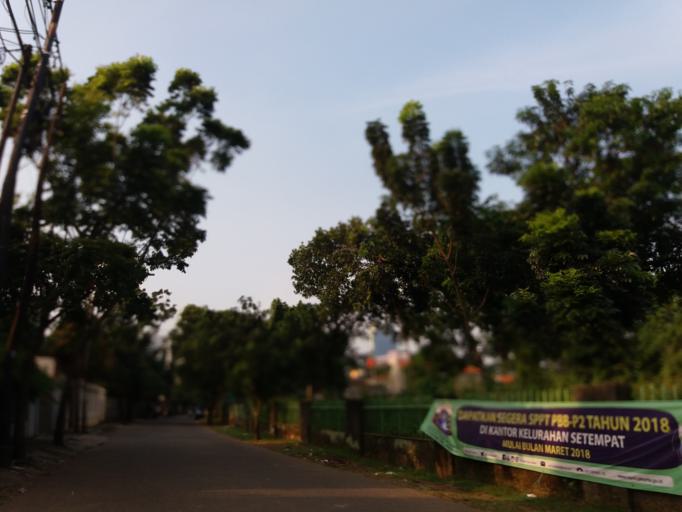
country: ID
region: Jakarta Raya
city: Jakarta
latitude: -6.2431
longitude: 106.8144
